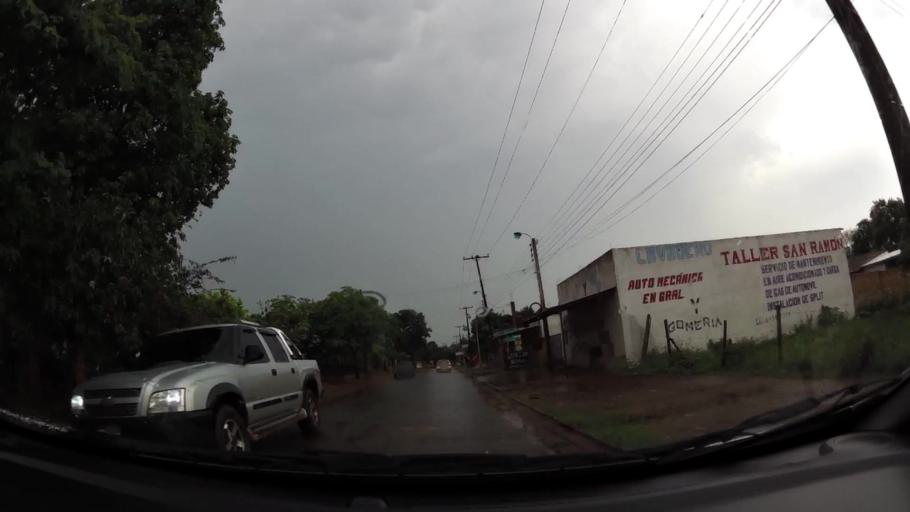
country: PY
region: Alto Parana
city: Presidente Franco
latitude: -25.5554
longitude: -54.6593
